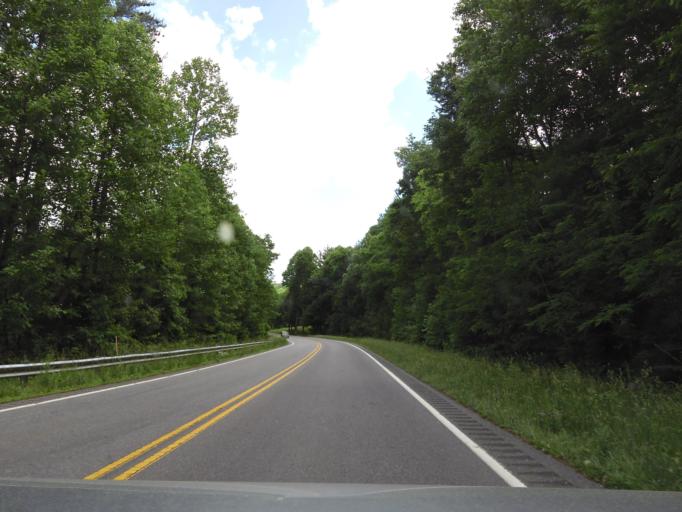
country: US
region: North Carolina
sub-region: Graham County
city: Robbinsville
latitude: 35.2696
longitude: -83.7211
